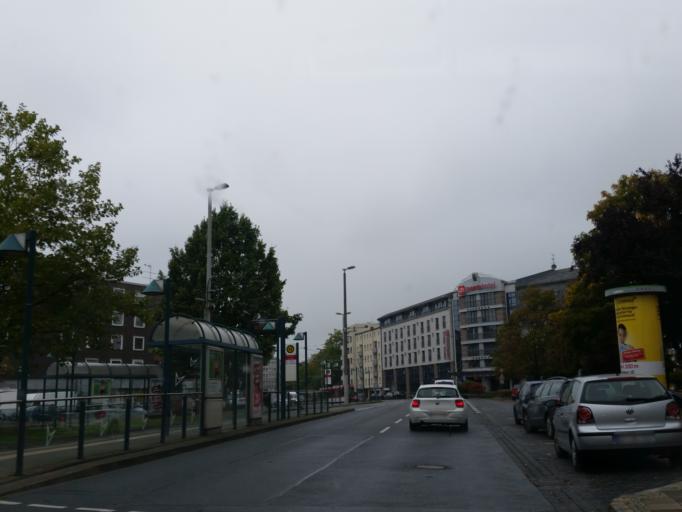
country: DE
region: Lower Saxony
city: Braunschweig
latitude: 52.2586
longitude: 10.5280
